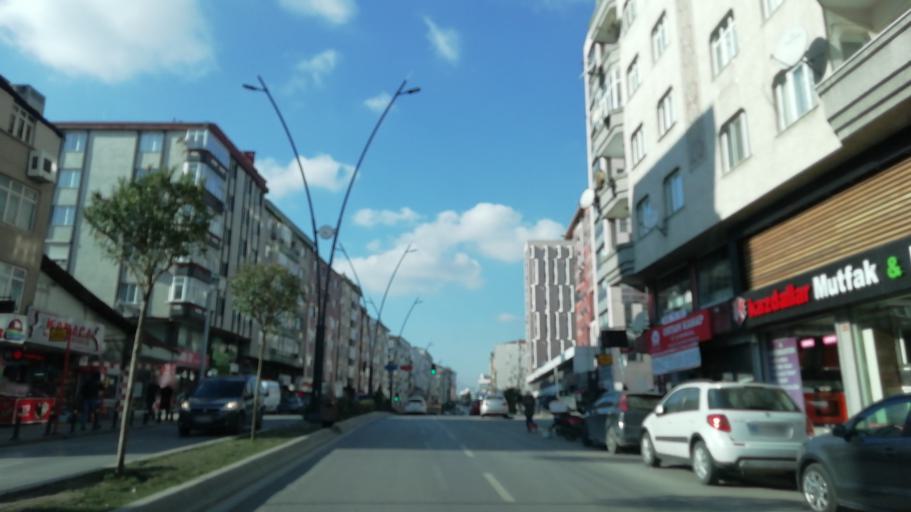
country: TR
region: Istanbul
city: Esenler
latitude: 41.0579
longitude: 28.9221
